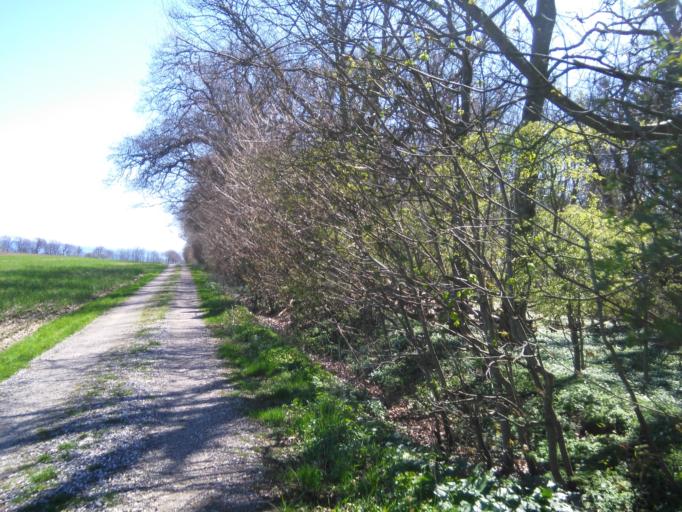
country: DK
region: Central Jutland
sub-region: Hedensted Kommune
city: Juelsminde
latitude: 55.7442
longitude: 10.0359
